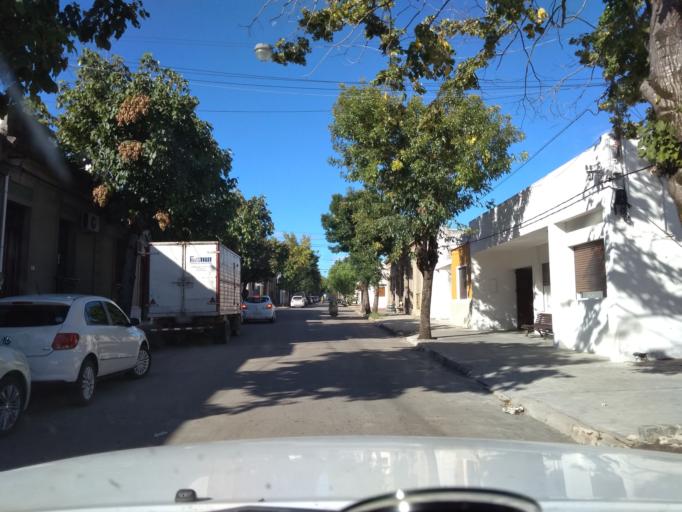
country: UY
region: Florida
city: Florida
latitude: -34.0989
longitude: -56.2192
